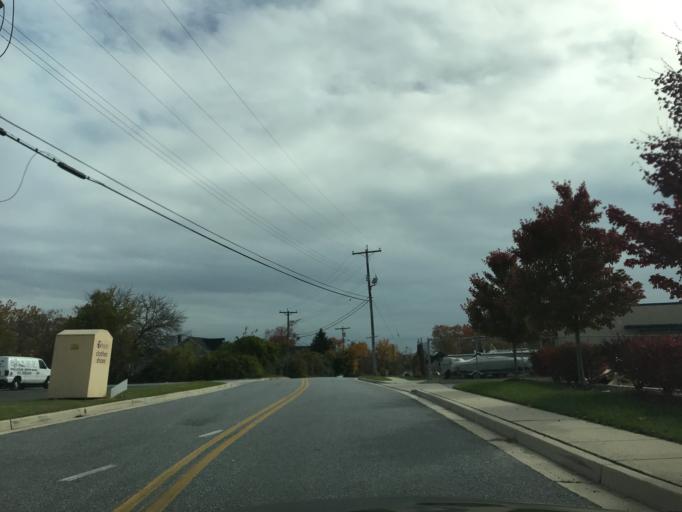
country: US
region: Maryland
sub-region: Baltimore County
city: Bowleys Quarters
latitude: 39.3348
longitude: -76.4118
